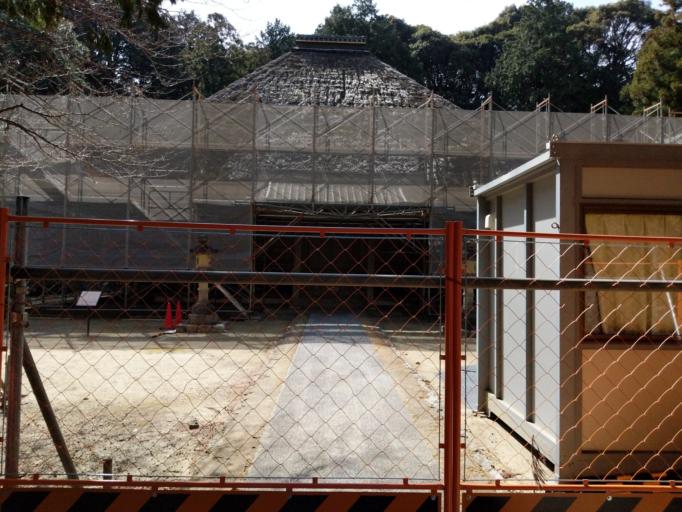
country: JP
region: Shizuoka
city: Kosai-shi
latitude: 34.7174
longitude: 137.5383
